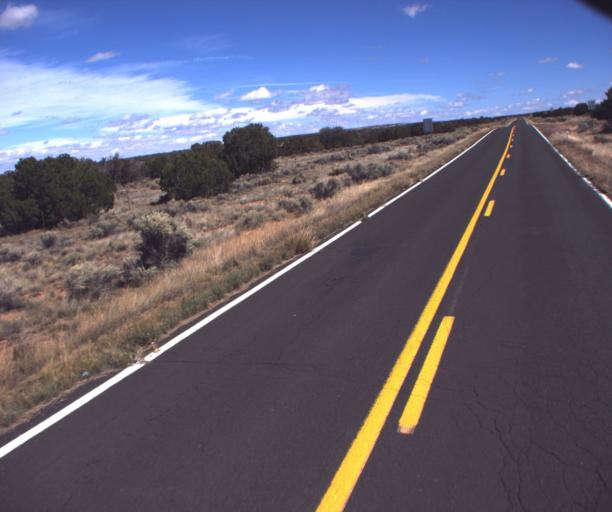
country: US
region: Arizona
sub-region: Apache County
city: Houck
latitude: 34.9042
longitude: -109.2347
